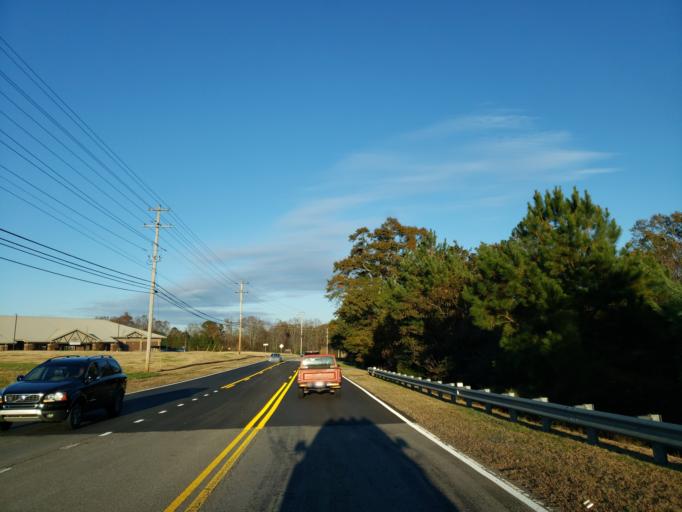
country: US
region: Georgia
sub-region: Cherokee County
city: Canton
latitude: 34.2125
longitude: -84.3958
